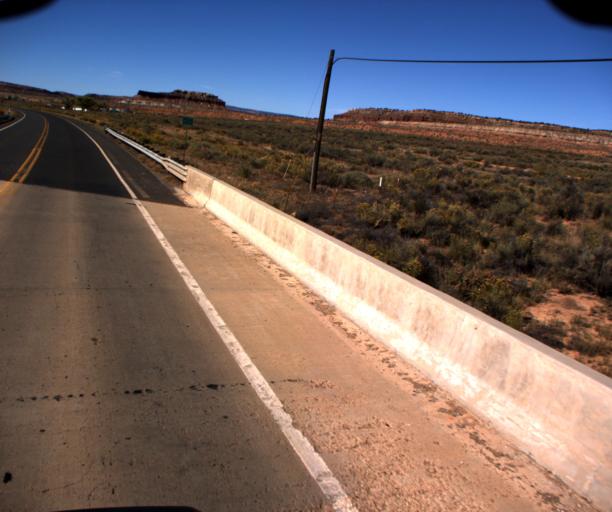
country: US
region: Arizona
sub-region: Coconino County
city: Fredonia
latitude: 36.9455
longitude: -112.5364
